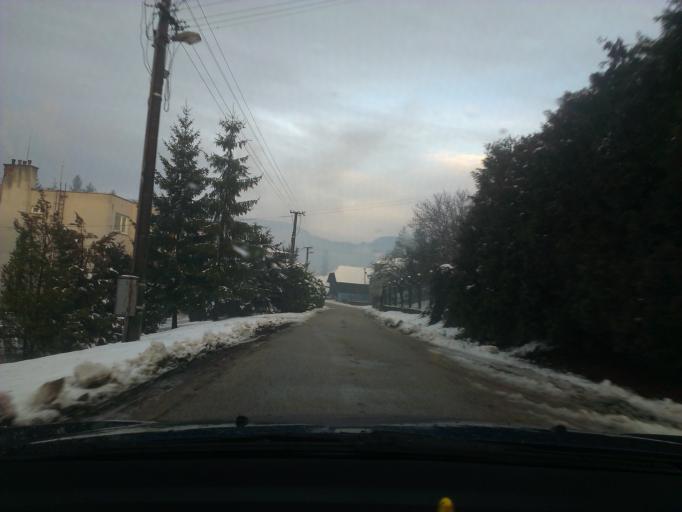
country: SK
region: Trnavsky
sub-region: Okres Trnava
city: Piestany
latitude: 48.6505
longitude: 17.9434
